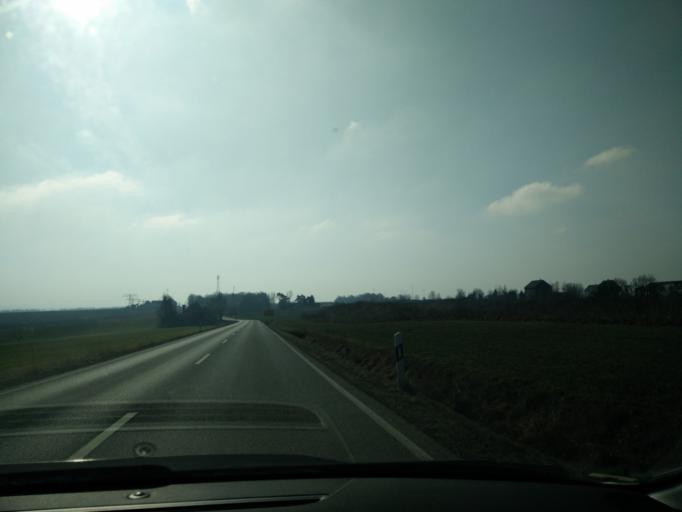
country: DE
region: Saxony
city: Penig
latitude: 50.9751
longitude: 12.6967
